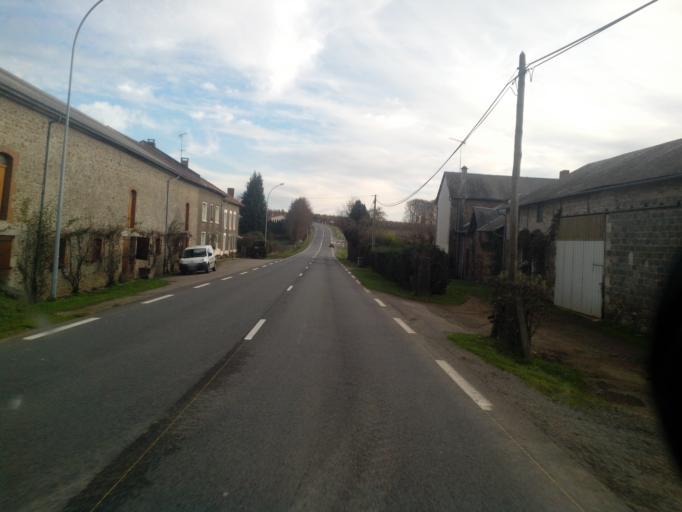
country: FR
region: Limousin
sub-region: Departement de la Haute-Vienne
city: Neuvic-Entier
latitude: 45.7345
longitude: 1.6137
